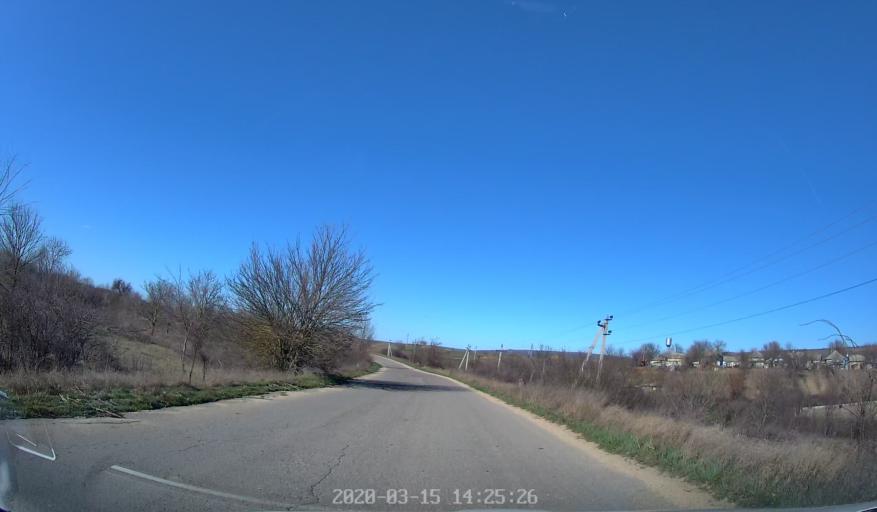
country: MD
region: Orhei
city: Orhei
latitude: 47.3381
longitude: 28.9170
